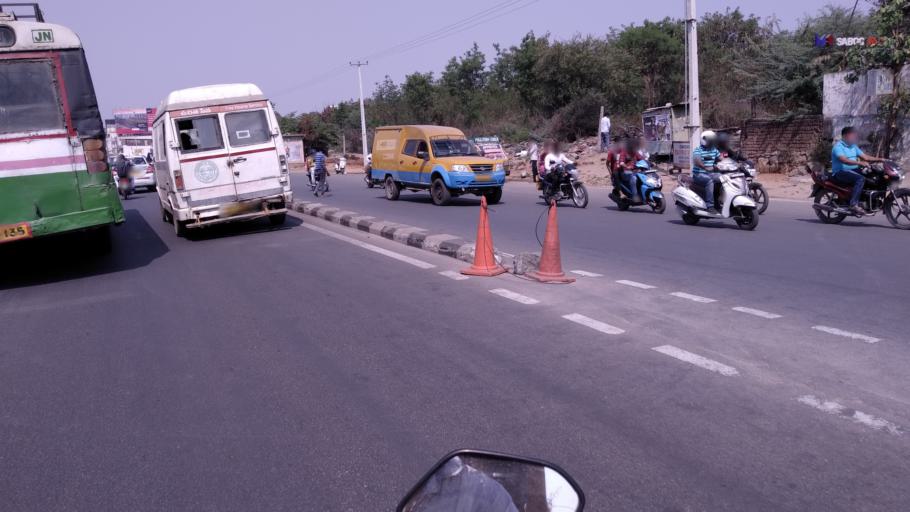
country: IN
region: Telangana
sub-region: Hyderabad
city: Malkajgiri
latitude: 17.4521
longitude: 78.4860
